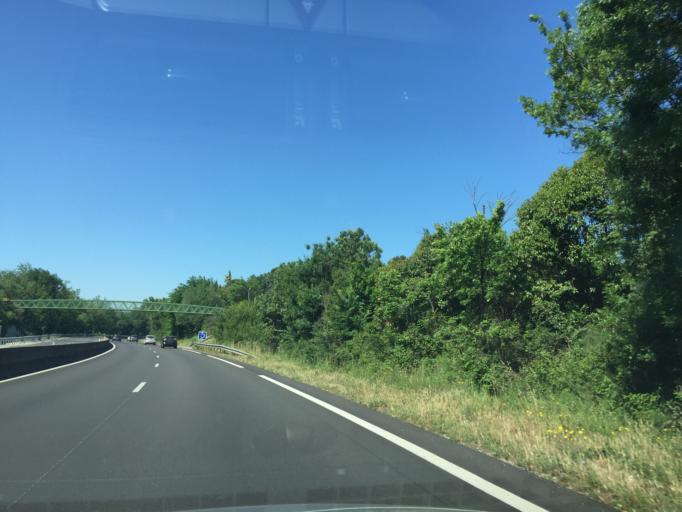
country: FR
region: Languedoc-Roussillon
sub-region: Departement du Gard
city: Les Angles
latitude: 43.9494
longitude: 4.7812
